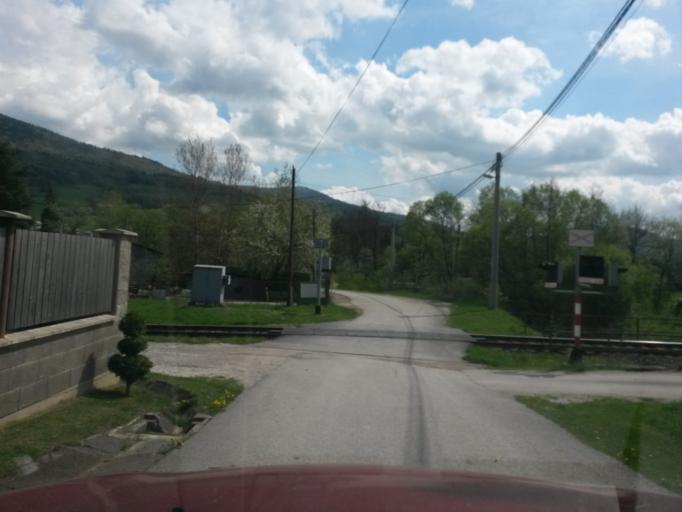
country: SK
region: Kosicky
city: Krompachy
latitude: 48.8098
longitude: 20.8094
